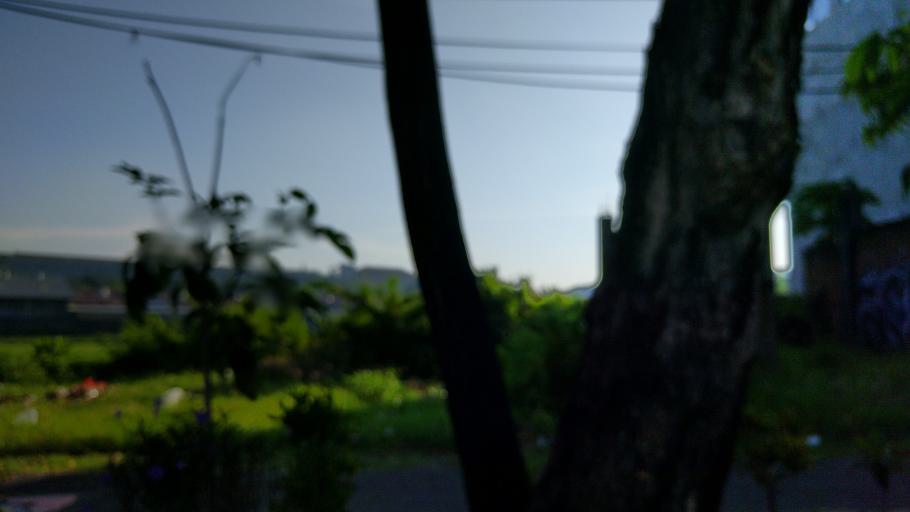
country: ID
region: Bali
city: Kuta
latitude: -8.7049
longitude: 115.1819
